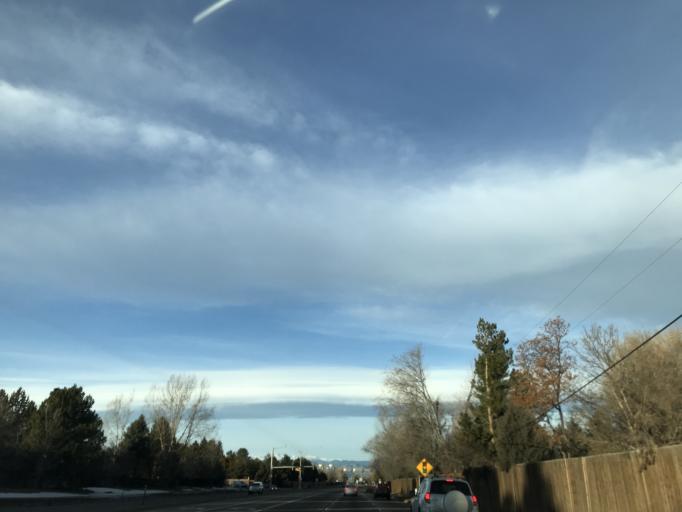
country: US
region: Colorado
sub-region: Arapahoe County
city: Cherry Hills Village
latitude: 39.6531
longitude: -104.9569
